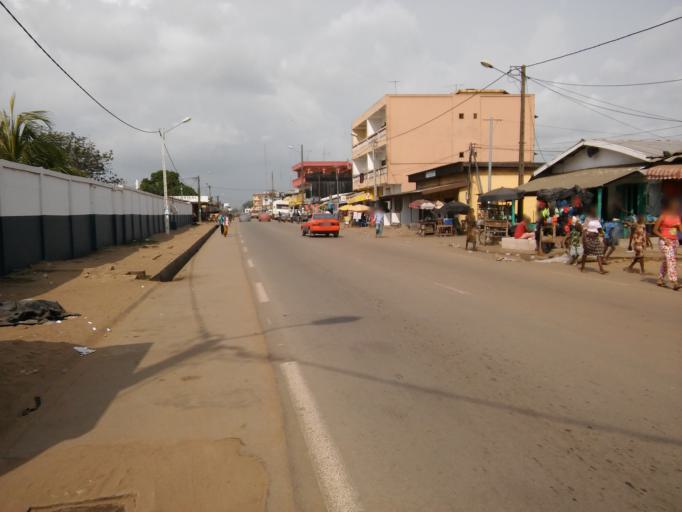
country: CI
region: Sud-Comoe
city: Grand-Bassam
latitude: 5.2074
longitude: -3.7351
